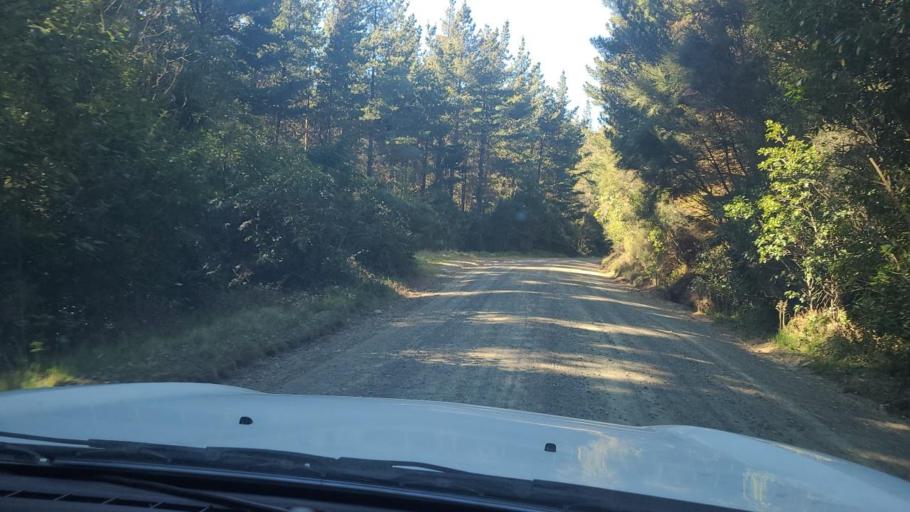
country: NZ
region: Hawke's Bay
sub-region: Napier City
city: Taradale
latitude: -39.4076
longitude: 176.4781
